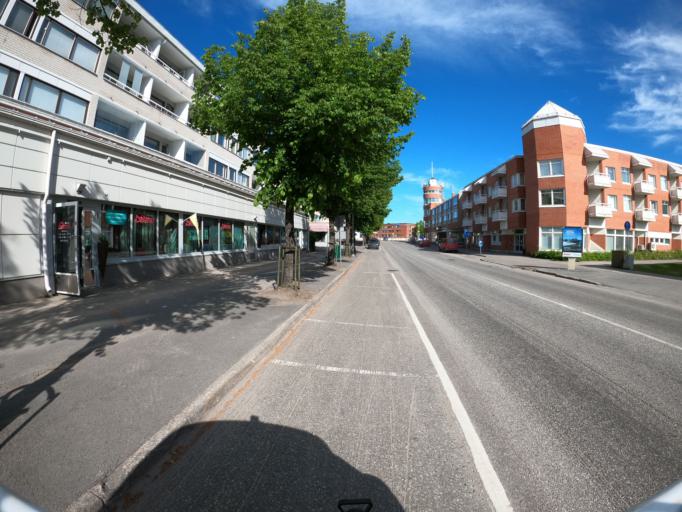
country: FI
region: Southern Savonia
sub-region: Savonlinna
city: Savonlinna
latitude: 61.8670
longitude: 28.8940
